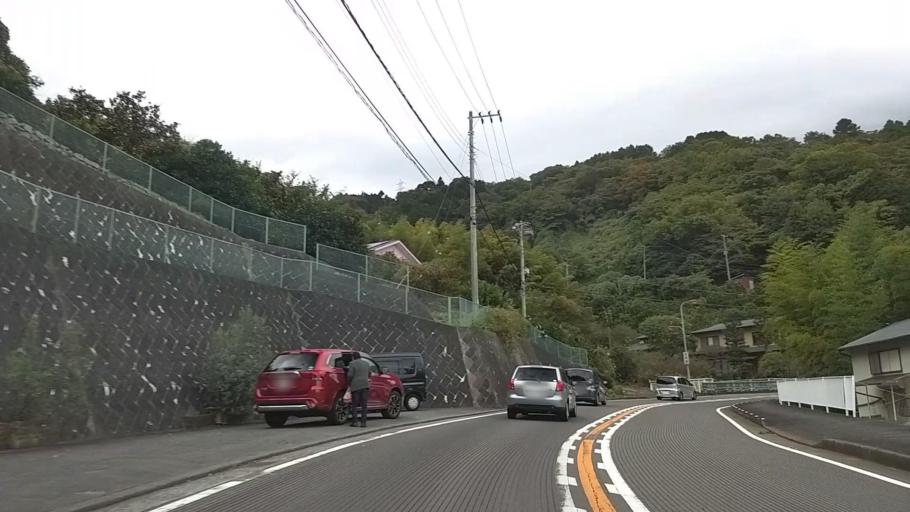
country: JP
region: Kanagawa
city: Yugawara
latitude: 35.1852
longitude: 139.1315
